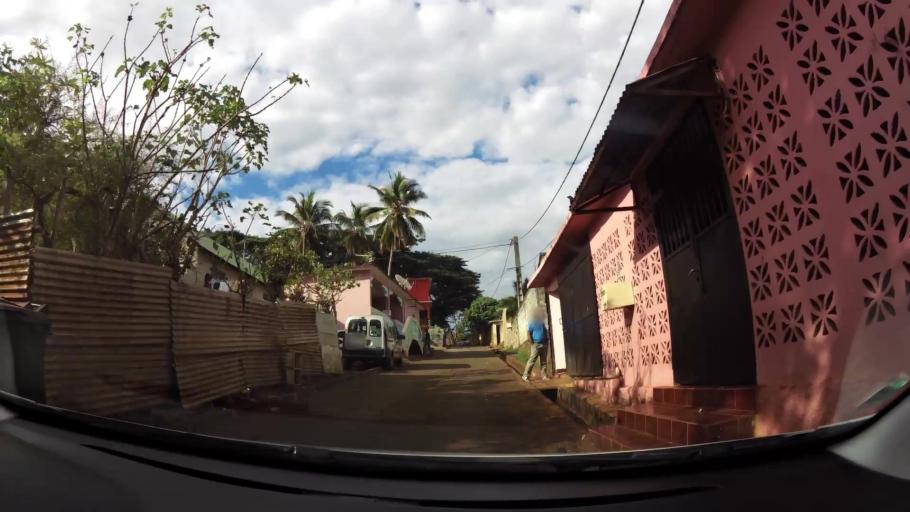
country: YT
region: Ouangani
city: Ouangani
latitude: -12.8364
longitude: 45.1317
